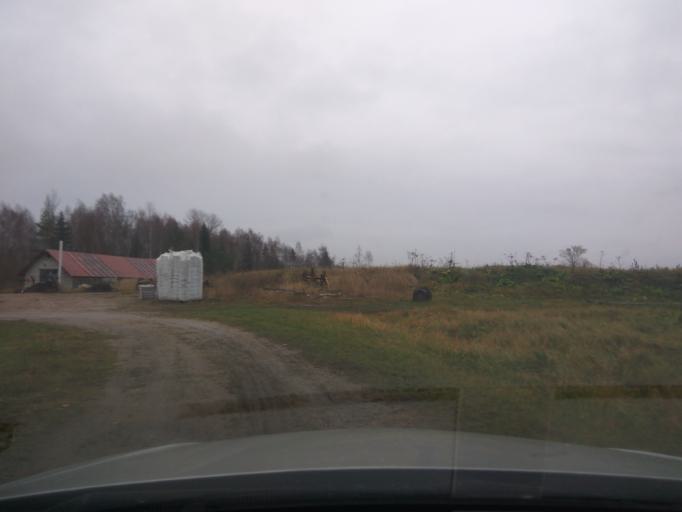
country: LV
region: Kuldigas Rajons
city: Kuldiga
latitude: 56.9309
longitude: 22.0107
